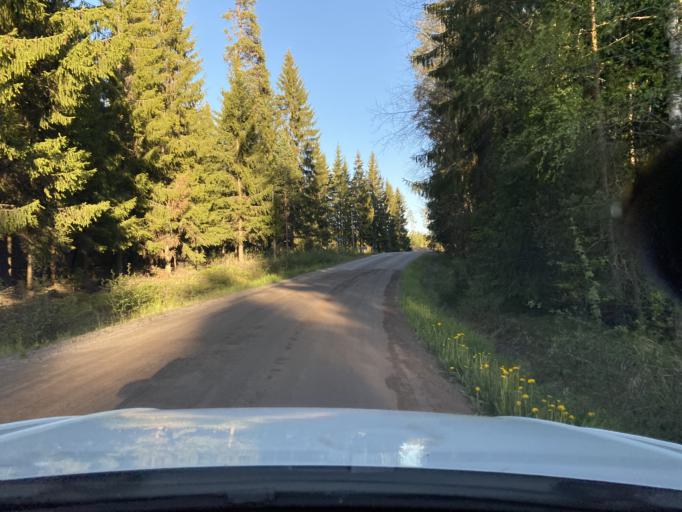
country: FI
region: Satakunta
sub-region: Rauma
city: Kiukainen
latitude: 61.1340
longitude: 21.9861
